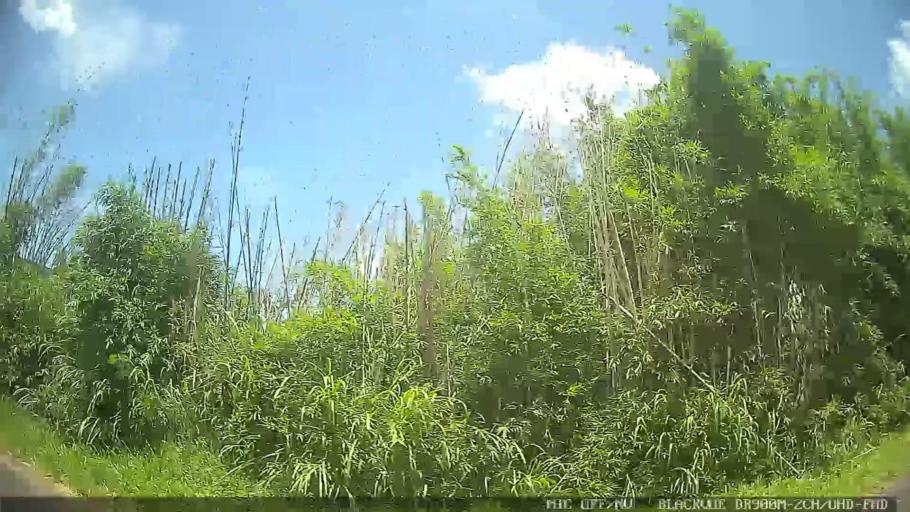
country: BR
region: Sao Paulo
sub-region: Laranjal Paulista
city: Laranjal Paulista
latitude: -23.0416
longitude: -47.8286
